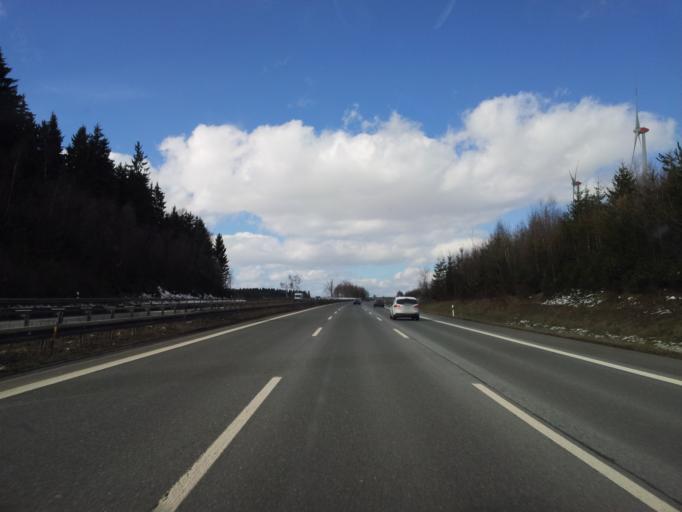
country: DE
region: Bavaria
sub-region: Upper Franconia
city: Gefrees
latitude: 50.1370
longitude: 11.7424
